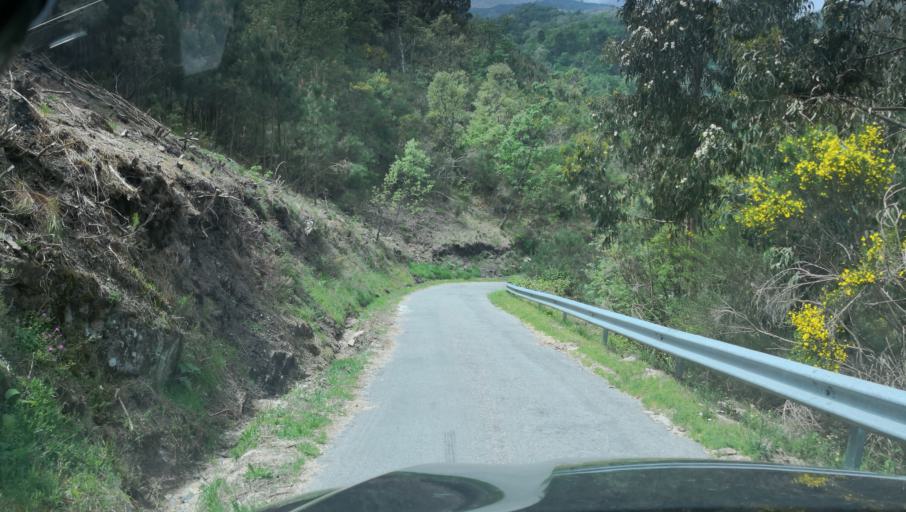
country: PT
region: Vila Real
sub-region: Vila Real
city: Vila Real
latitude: 41.3105
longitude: -7.7991
